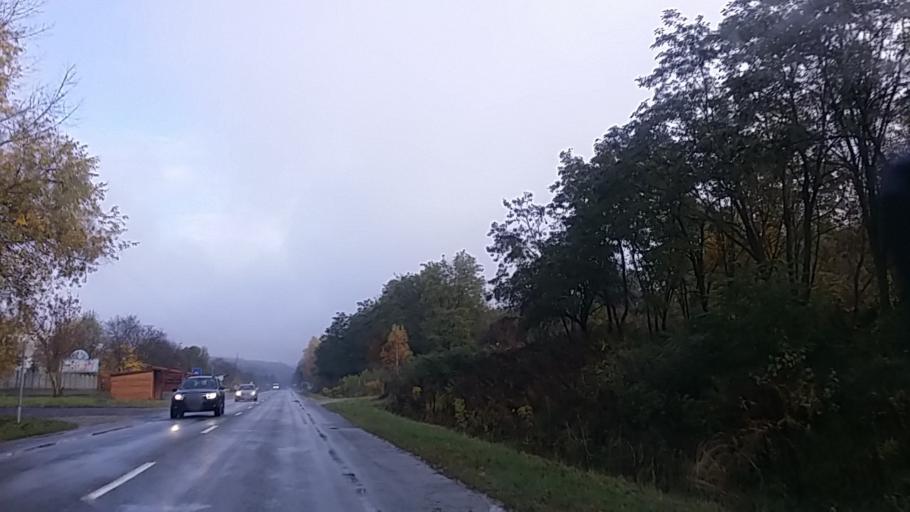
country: HU
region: Heves
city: Belapatfalva
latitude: 48.0655
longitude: 20.3556
